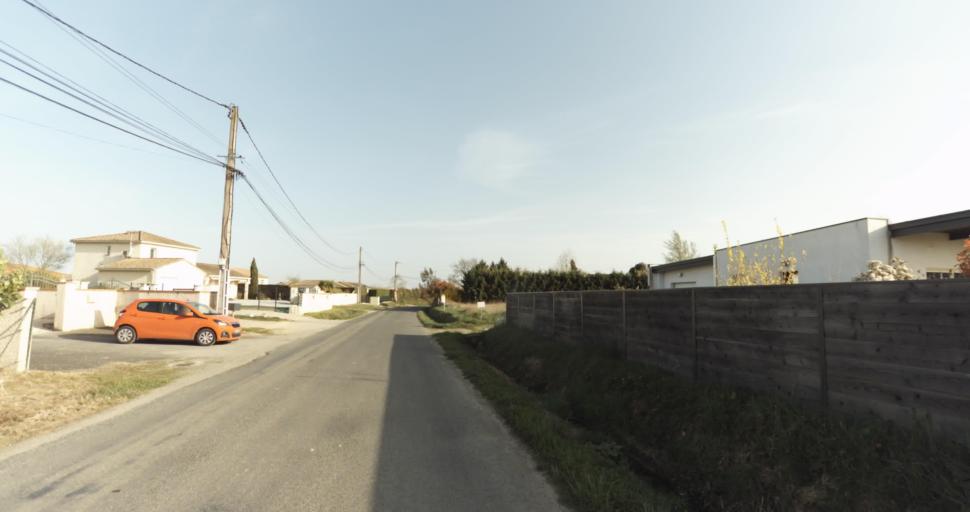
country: FR
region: Midi-Pyrenees
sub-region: Departement du Tarn
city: Saint-Sulpice-la-Pointe
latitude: 43.7571
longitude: 1.6875
